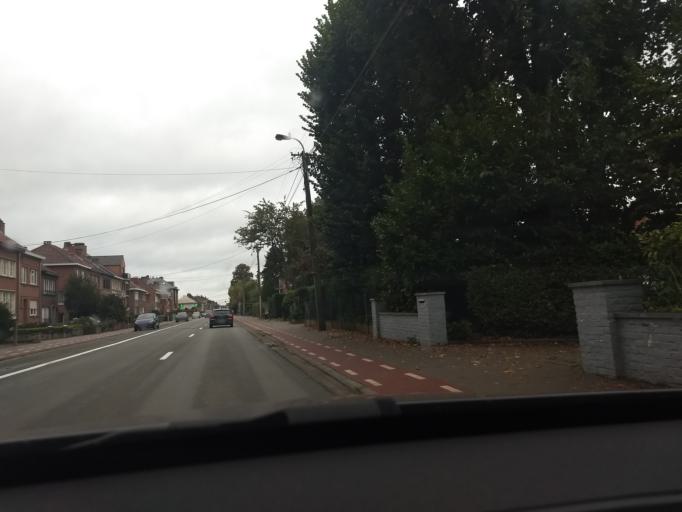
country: BE
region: Wallonia
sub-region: Province du Brabant Wallon
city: Braine-l'Alleud
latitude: 50.6763
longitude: 4.3816
